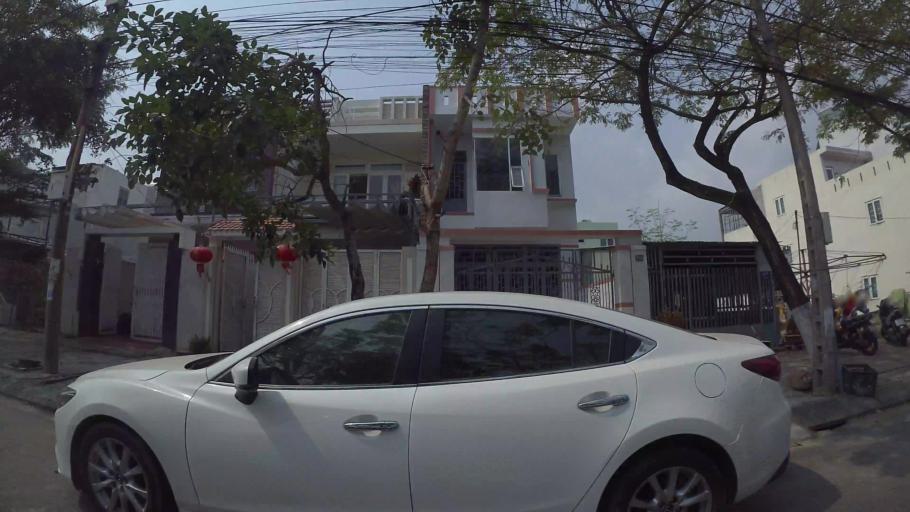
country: VN
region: Da Nang
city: Da Nang
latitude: 16.0953
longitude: 108.2297
